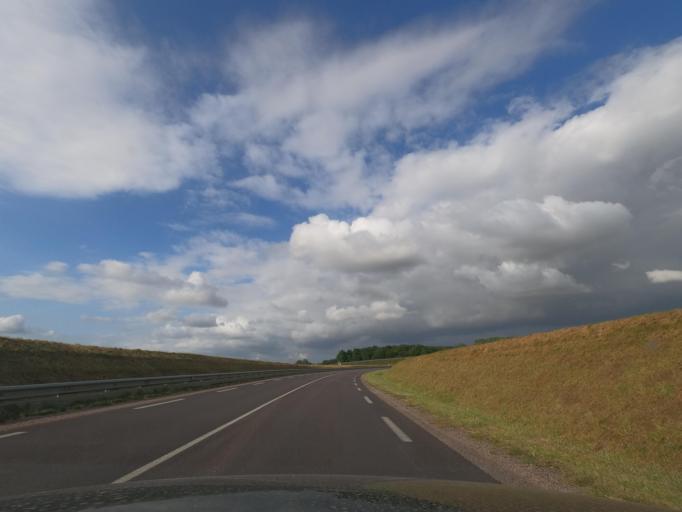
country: FR
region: Haute-Normandie
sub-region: Departement de l'Eure
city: Bernay
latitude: 49.1026
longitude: 0.5755
